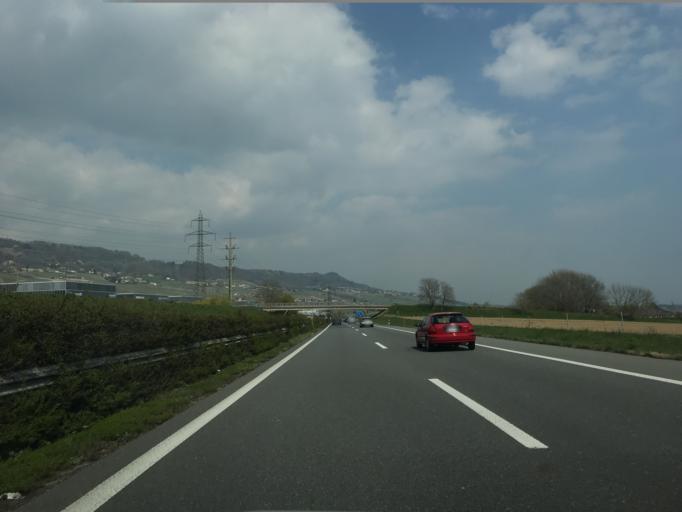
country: CH
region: Vaud
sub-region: Nyon District
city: Rolle
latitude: 46.4573
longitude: 6.3193
